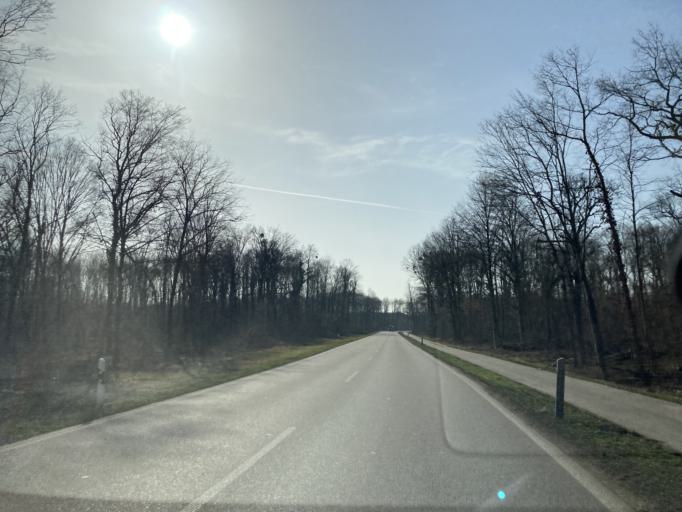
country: DE
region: Baden-Wuerttemberg
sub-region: Freiburg Region
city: Hartheim
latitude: 47.9091
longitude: 7.5980
